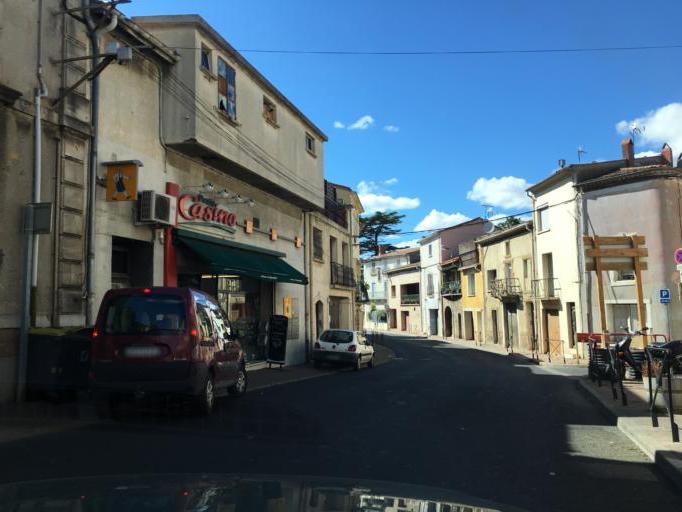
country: FR
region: Languedoc-Roussillon
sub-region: Departement de l'Herault
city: Florensac
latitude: 43.3832
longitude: 3.4658
